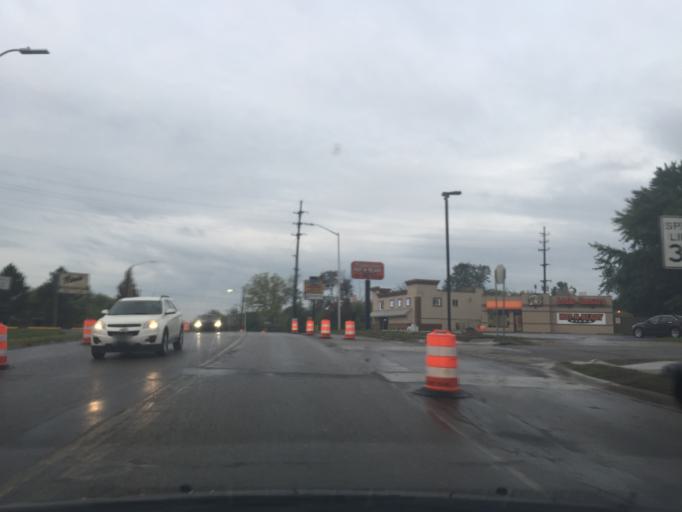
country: US
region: Michigan
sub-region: Oakland County
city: Pontiac
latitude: 42.6487
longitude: -83.2864
